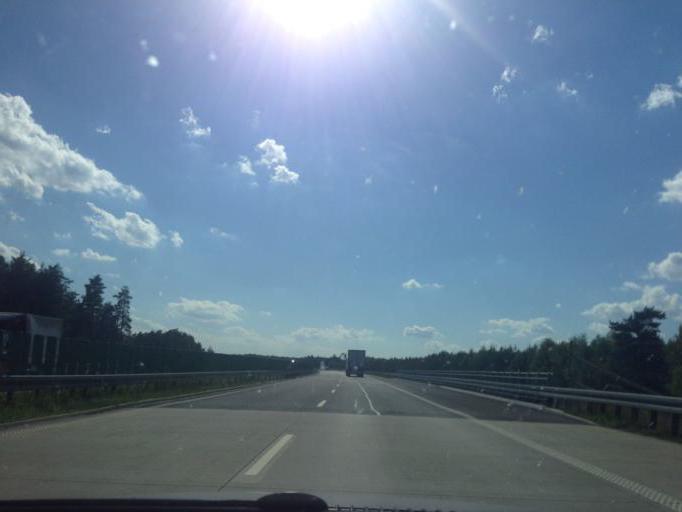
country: PL
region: Lower Silesian Voivodeship
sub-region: Powiat boleslawiecki
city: Nowogrodziec
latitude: 51.2705
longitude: 15.3902
